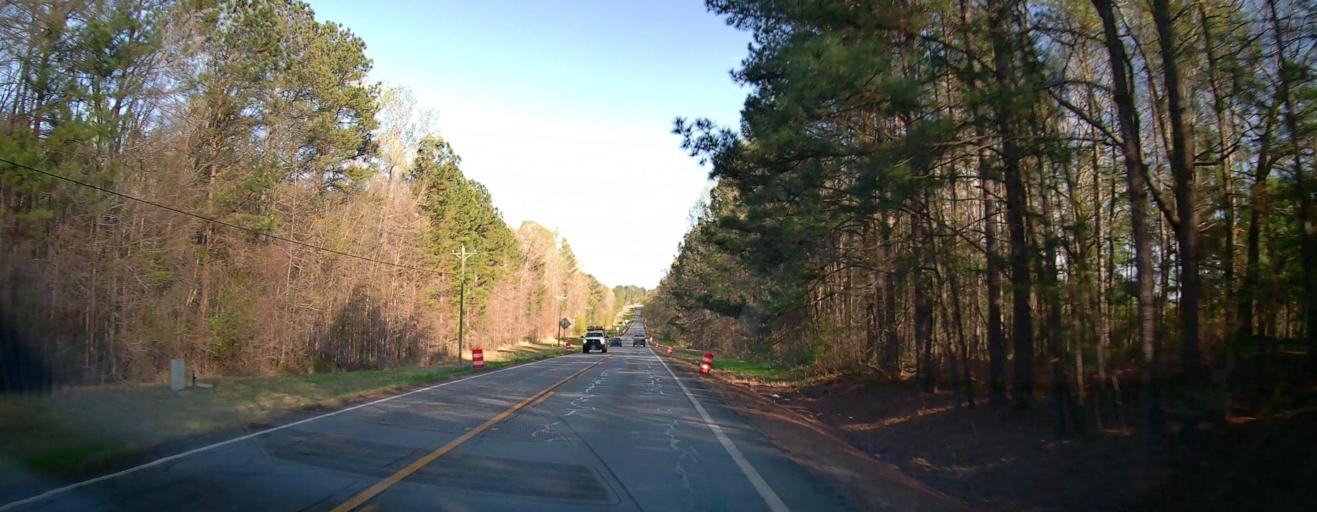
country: US
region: Georgia
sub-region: Putnam County
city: Eatonton
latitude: 33.1754
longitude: -83.4006
